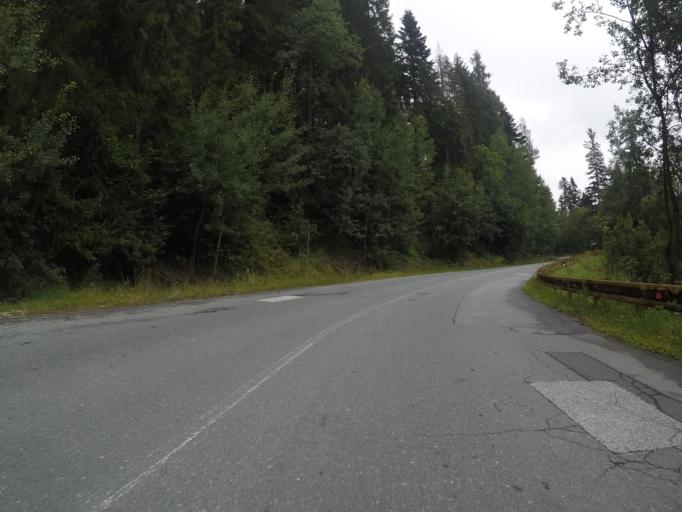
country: SK
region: Kosicky
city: Spisska Nova Ves
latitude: 48.8768
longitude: 20.5221
